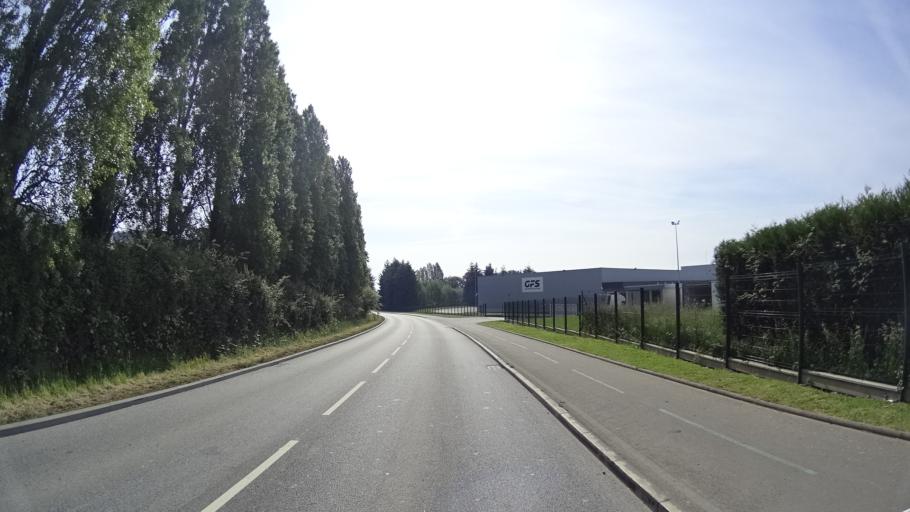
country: FR
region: Brittany
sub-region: Departement d'Ille-et-Vilaine
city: Noyal-sur-Vilaine
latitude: 48.1063
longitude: -1.5294
